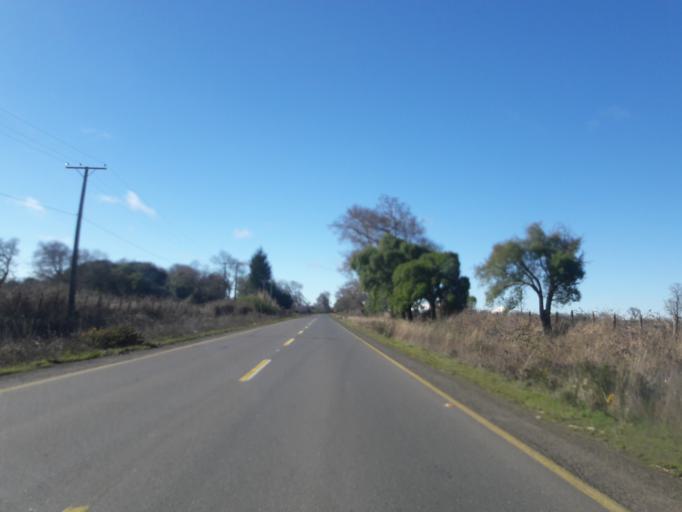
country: CL
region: Araucania
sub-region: Provincia de Malleco
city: Victoria
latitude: -38.2537
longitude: -72.2880
